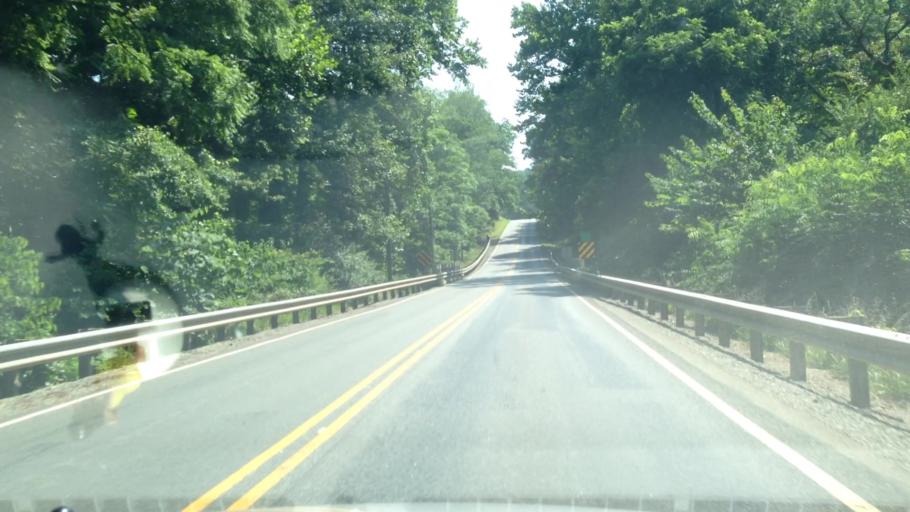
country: US
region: Virginia
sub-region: Patrick County
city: Stuart
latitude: 36.5947
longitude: -80.3132
